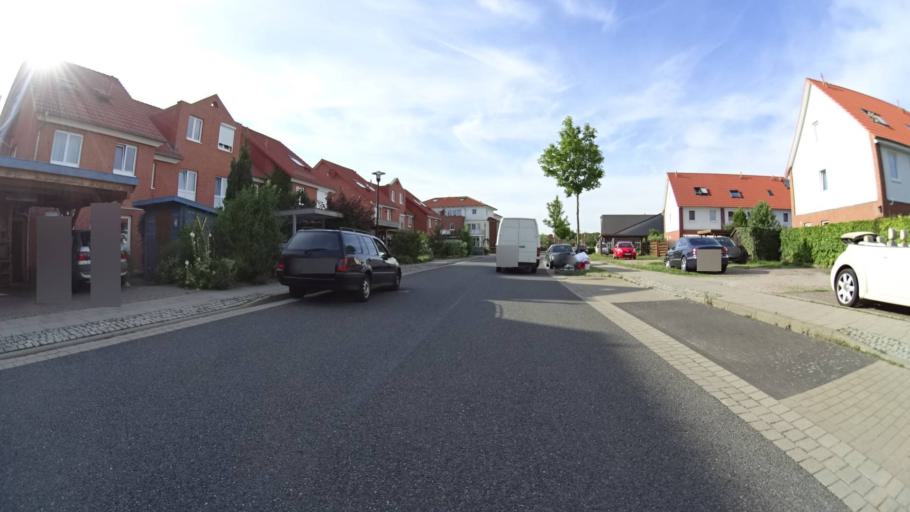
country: DE
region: Lower Saxony
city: Lueneburg
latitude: 53.2369
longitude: 10.3841
